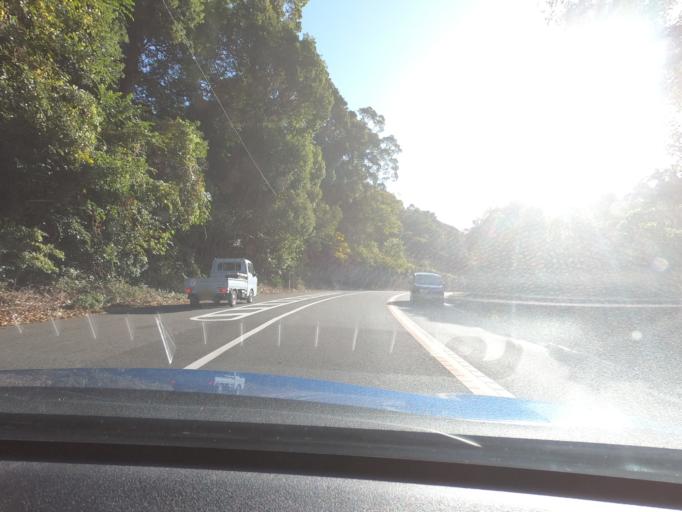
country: JP
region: Kumamoto
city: Minamata
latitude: 32.1636
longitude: 130.3754
